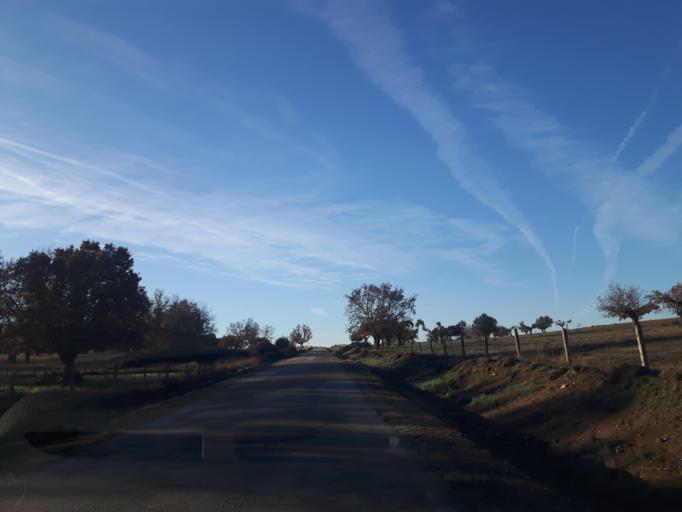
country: ES
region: Castille and Leon
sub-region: Provincia de Salamanca
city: Cerralbo
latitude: 40.9661
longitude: -6.5919
